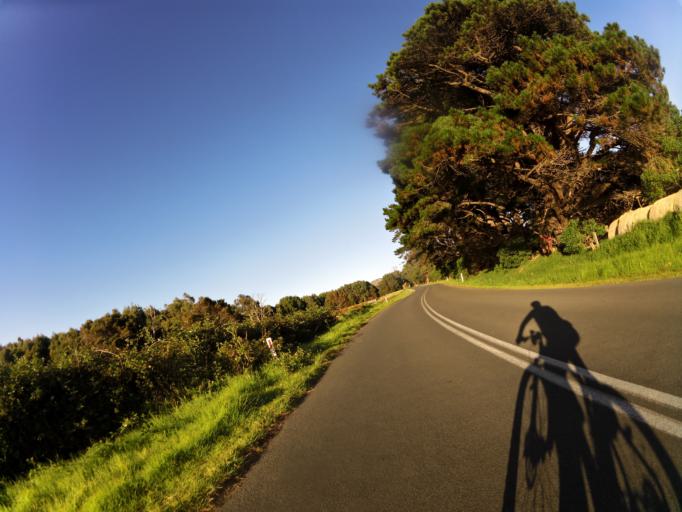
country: AU
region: Victoria
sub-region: Colac-Otway
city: Apollo Bay
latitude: -38.7672
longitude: 143.6573
